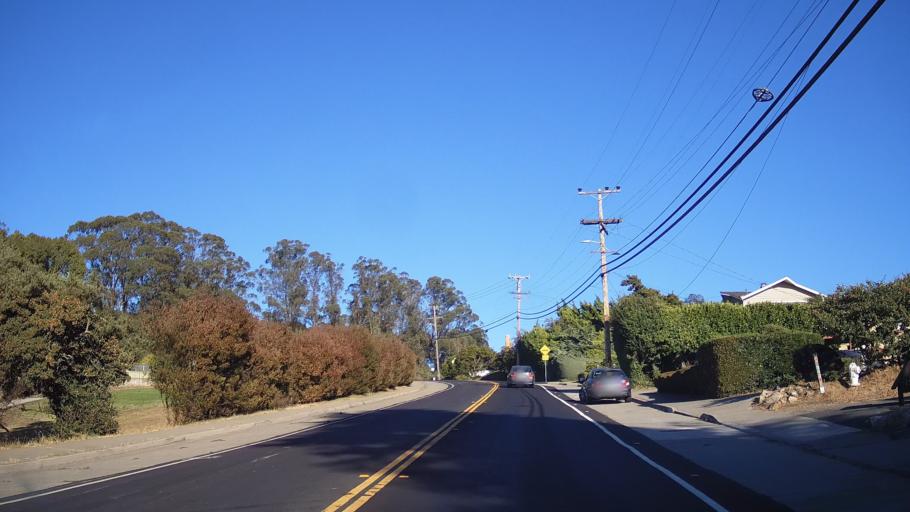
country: US
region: California
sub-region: Contra Costa County
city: El Cerrito
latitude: 37.9296
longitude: -122.3015
